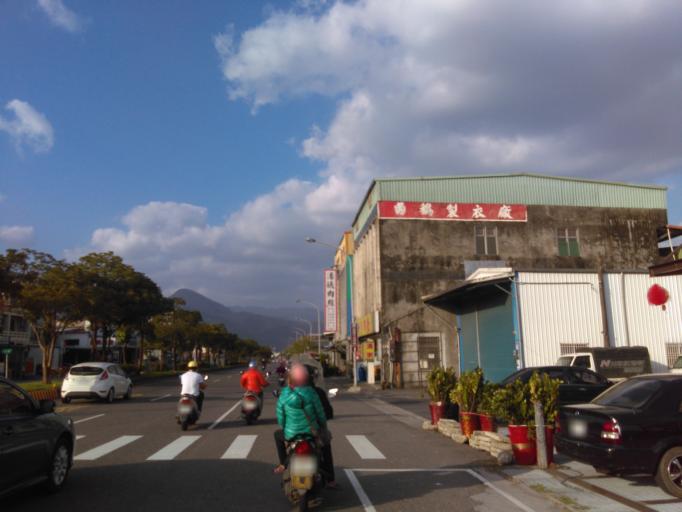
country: TW
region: Taiwan
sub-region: Yilan
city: Yilan
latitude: 24.7984
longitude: 121.7643
